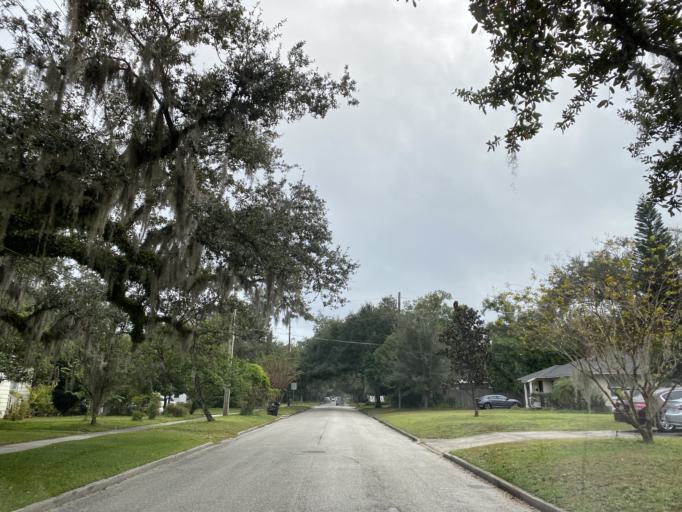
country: US
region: Florida
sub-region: Orange County
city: Fairview Shores
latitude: 28.5639
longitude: -81.3968
